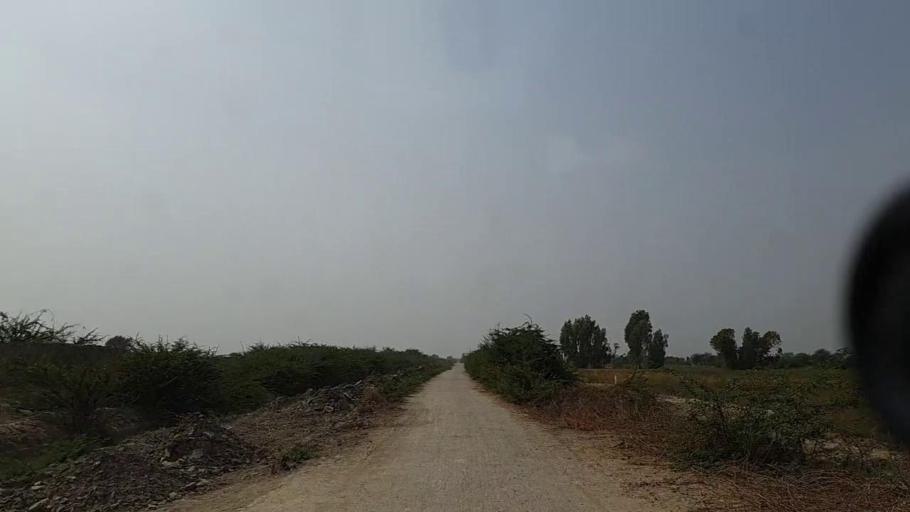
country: PK
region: Sindh
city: Naukot
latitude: 24.7721
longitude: 69.3156
